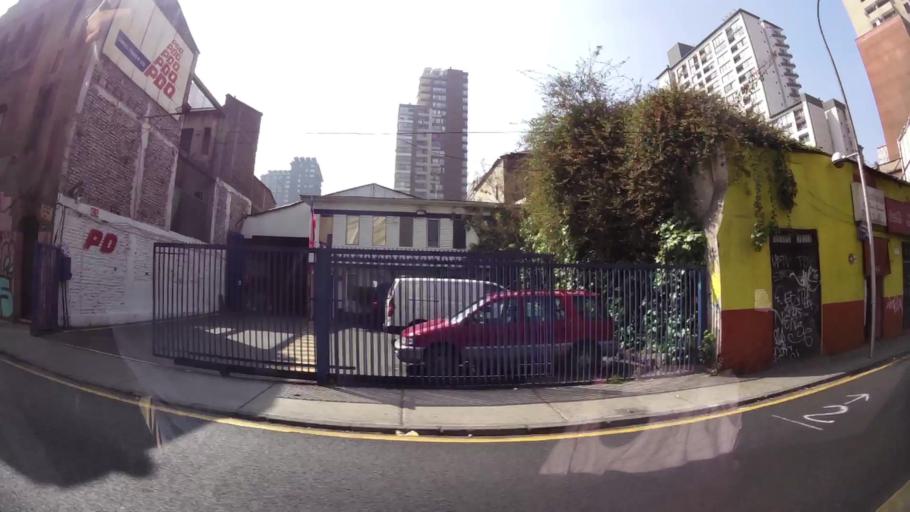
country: CL
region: Santiago Metropolitan
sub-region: Provincia de Santiago
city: Santiago
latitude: -33.4477
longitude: -70.6448
